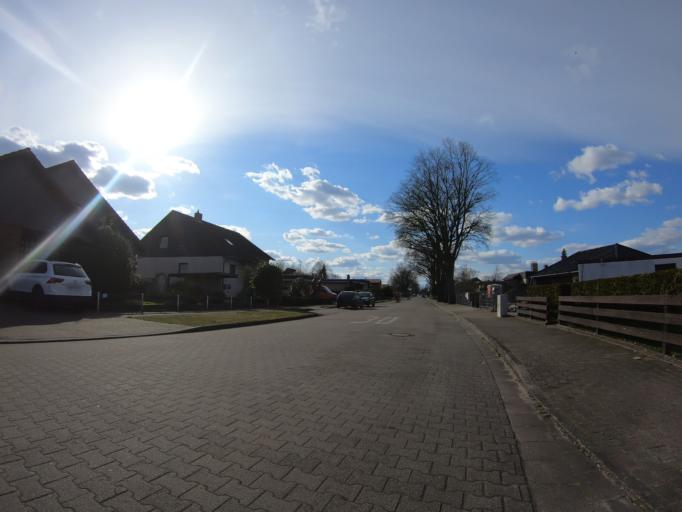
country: DE
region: Lower Saxony
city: Wesendorf
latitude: 52.5888
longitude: 10.5426
